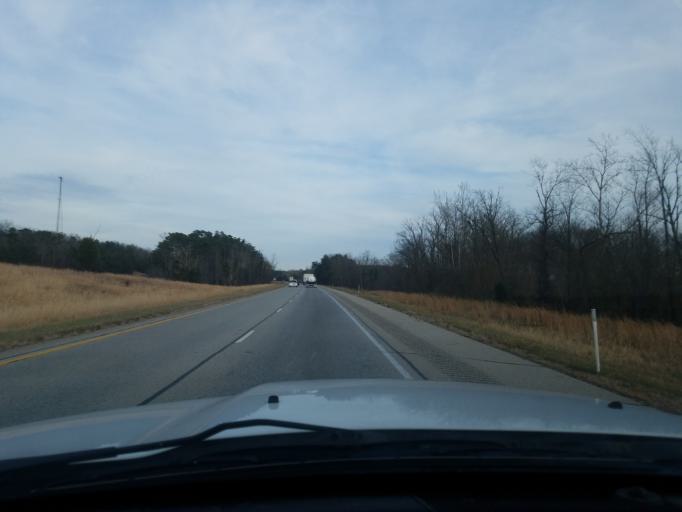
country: US
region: Indiana
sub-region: Floyd County
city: Georgetown
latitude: 38.2730
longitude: -85.9657
